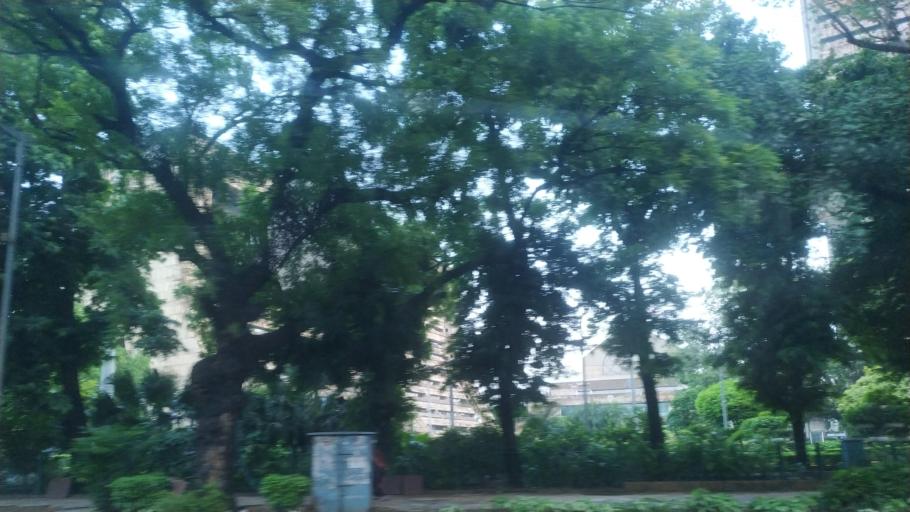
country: IN
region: NCT
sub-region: New Delhi
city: New Delhi
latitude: 28.6274
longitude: 77.2157
